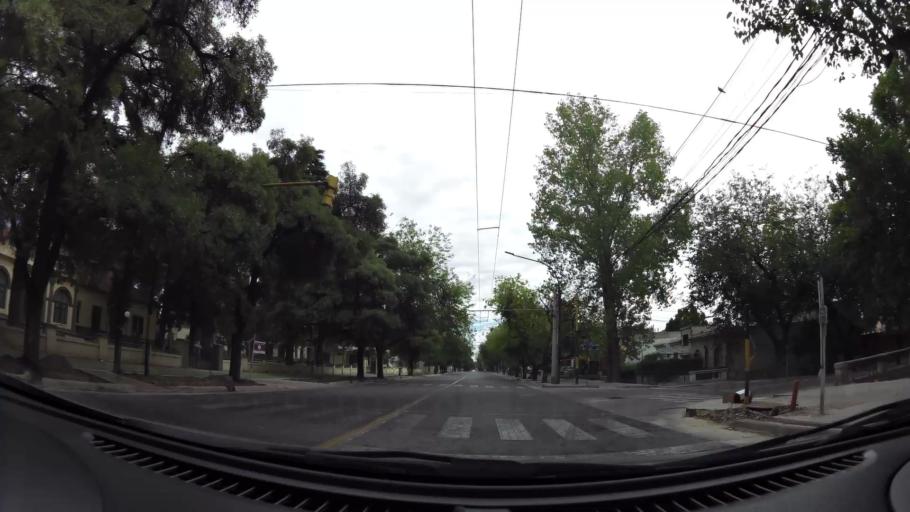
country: AR
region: Mendoza
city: Mendoza
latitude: -32.8801
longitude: -68.8599
